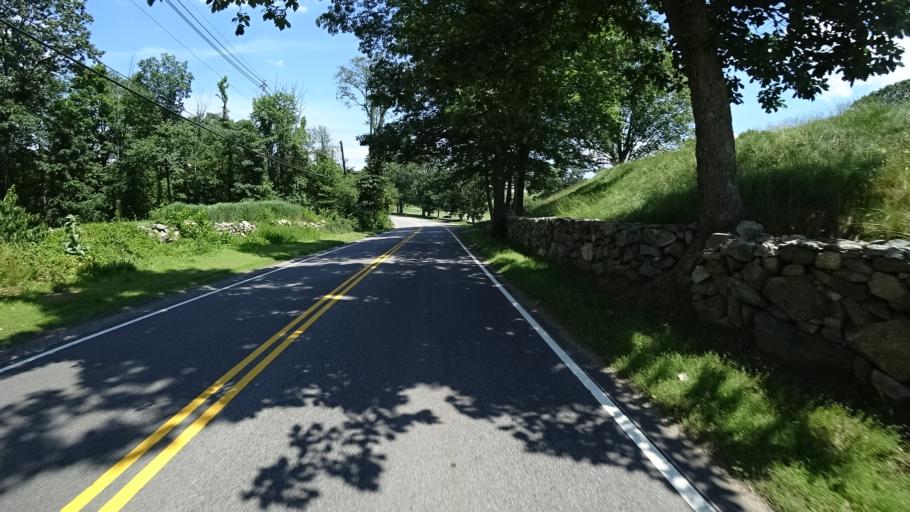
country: US
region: Massachusetts
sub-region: Norfolk County
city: Needham
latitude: 42.2536
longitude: -71.2240
